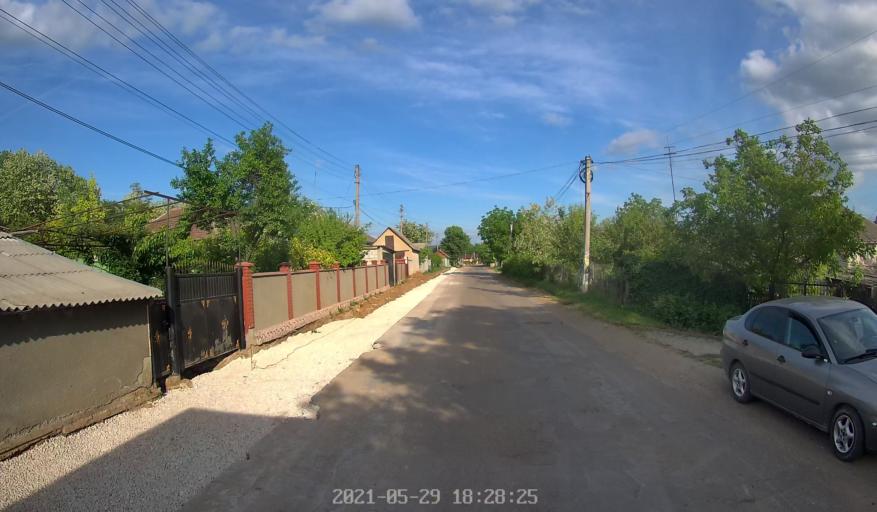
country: MD
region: Chisinau
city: Singera
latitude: 46.8288
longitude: 28.8663
